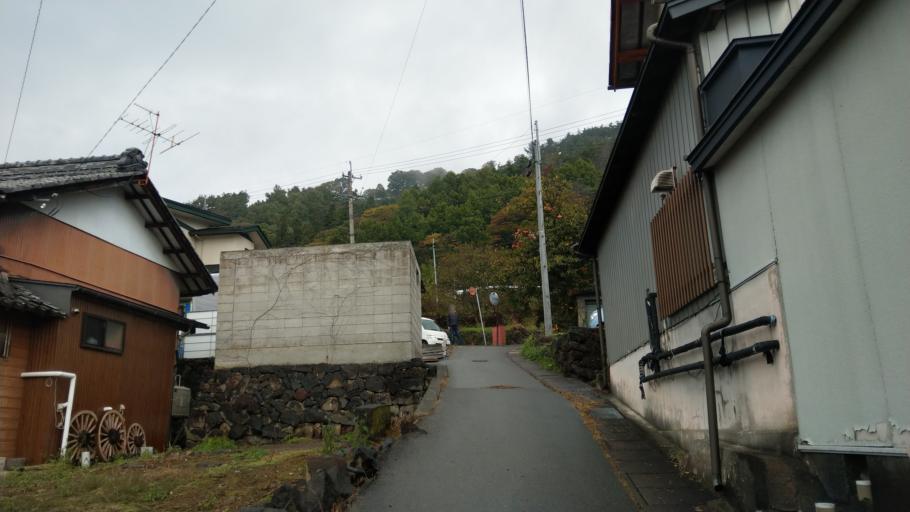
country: JP
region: Nagano
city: Komoro
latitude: 36.3418
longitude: 138.4169
